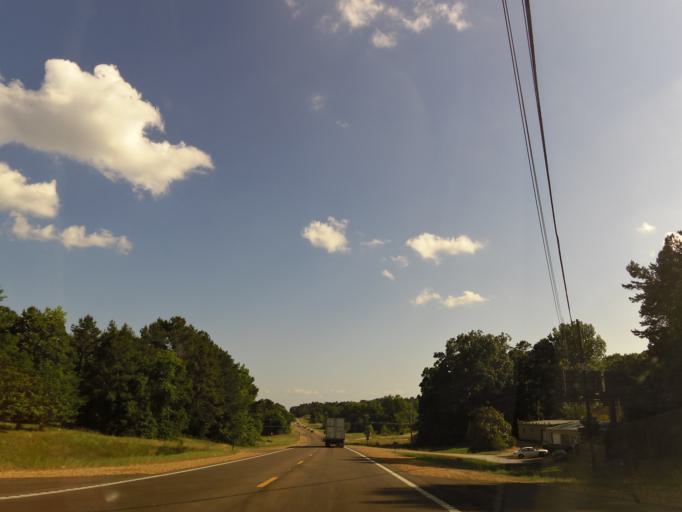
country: US
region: Mississippi
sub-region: Lafayette County
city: University
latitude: 34.3125
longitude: -89.5196
